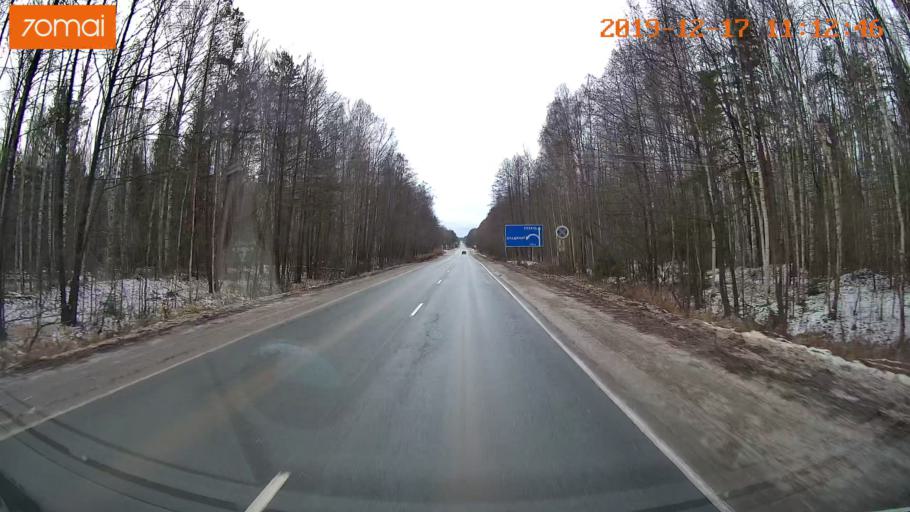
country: RU
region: Vladimir
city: Gus'-Khrustal'nyy
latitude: 55.5716
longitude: 40.6252
